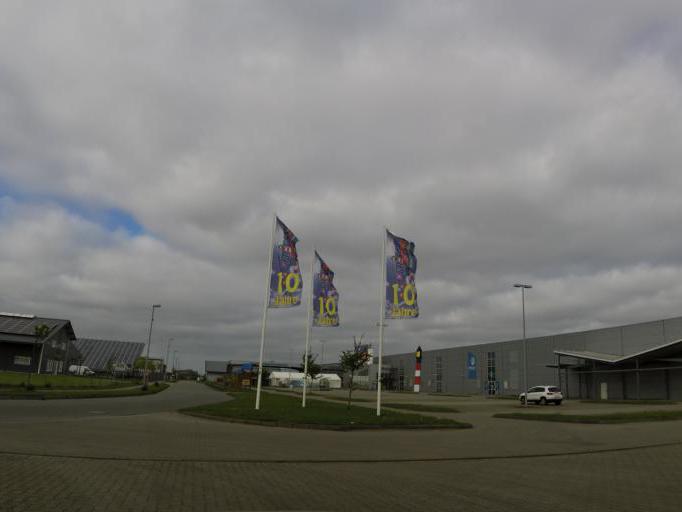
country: DE
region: Schleswig-Holstein
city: Niebull
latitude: 54.7823
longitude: 8.8518
